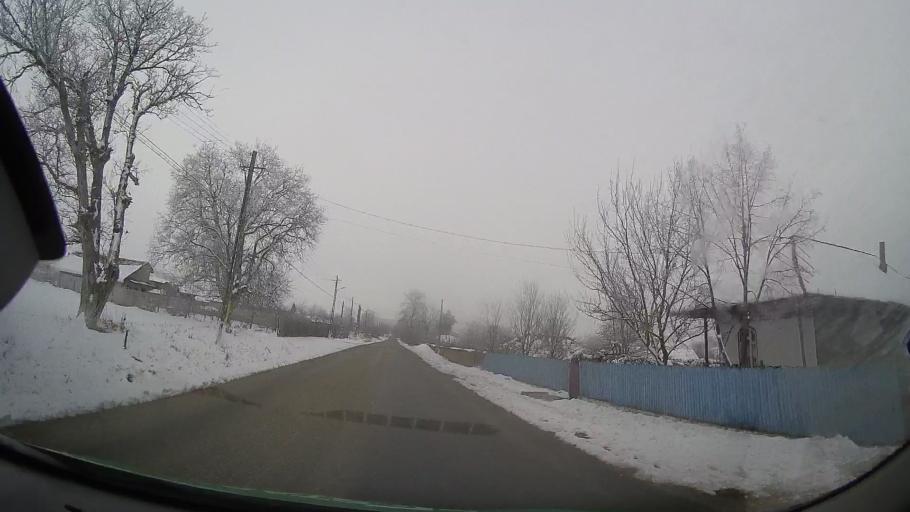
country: RO
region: Bacau
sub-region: Comuna Oncesti
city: Oncesti
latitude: 46.4444
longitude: 27.2654
